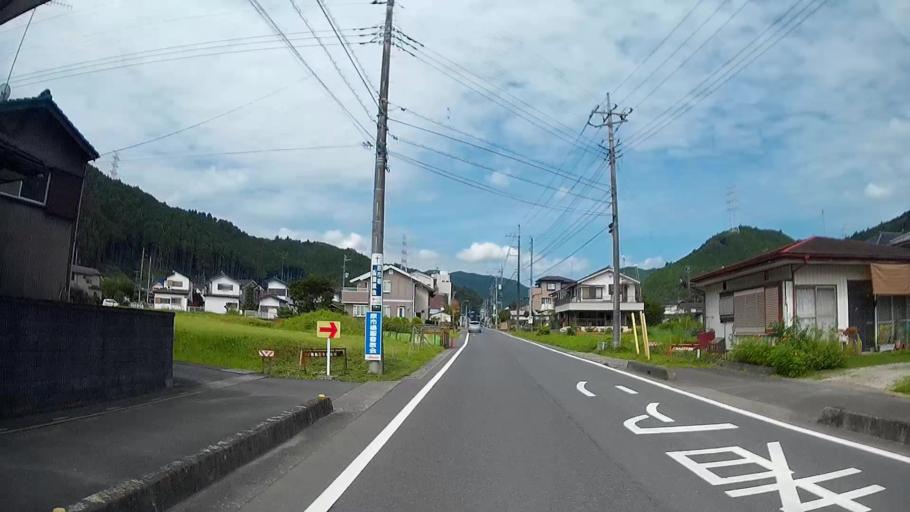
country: JP
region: Saitama
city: Hanno
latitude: 35.8679
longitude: 139.2503
